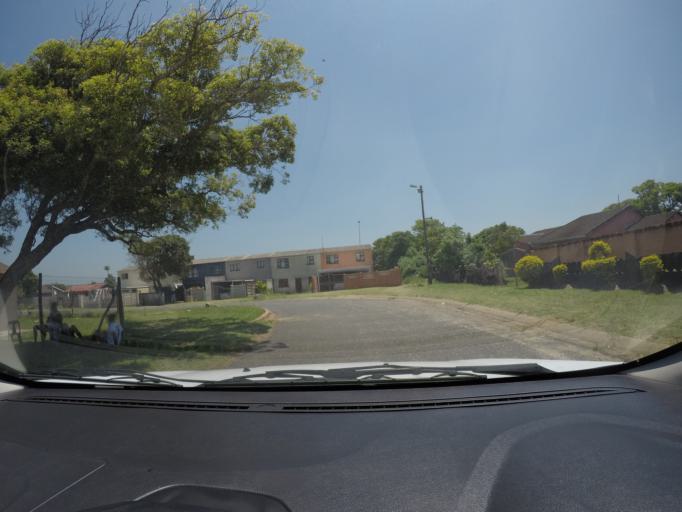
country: ZA
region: KwaZulu-Natal
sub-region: uThungulu District Municipality
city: eSikhawini
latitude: -28.8757
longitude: 31.9088
